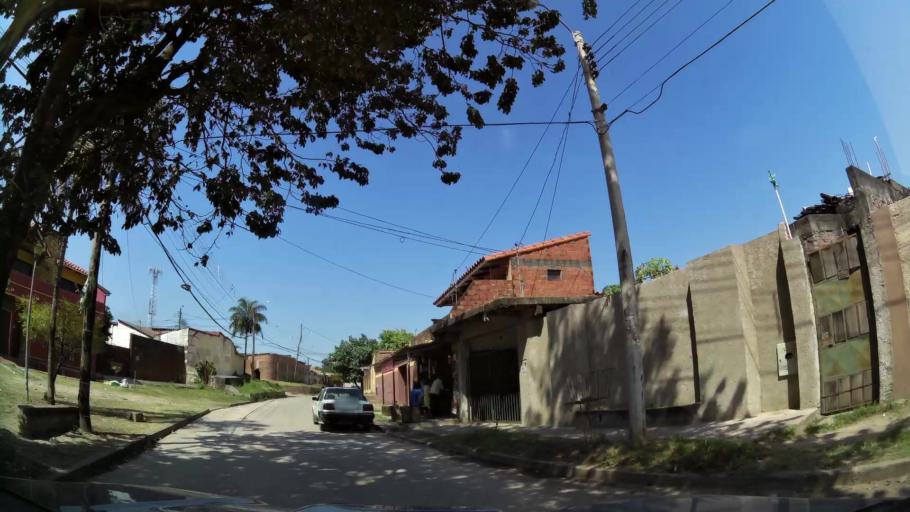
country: BO
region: Santa Cruz
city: Santa Cruz de la Sierra
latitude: -17.7451
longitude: -63.1810
